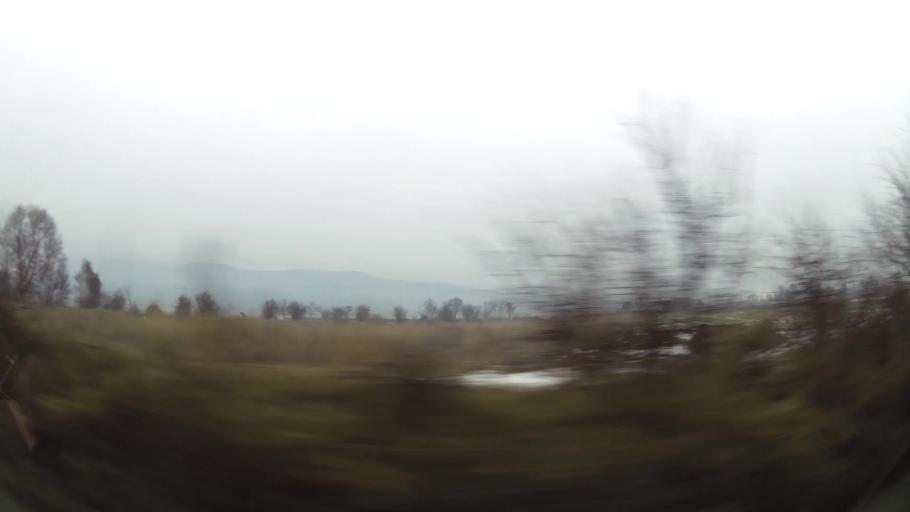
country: MK
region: Cucer-Sandevo
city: Chucher - Sandevo
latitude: 42.0648
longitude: 21.3689
